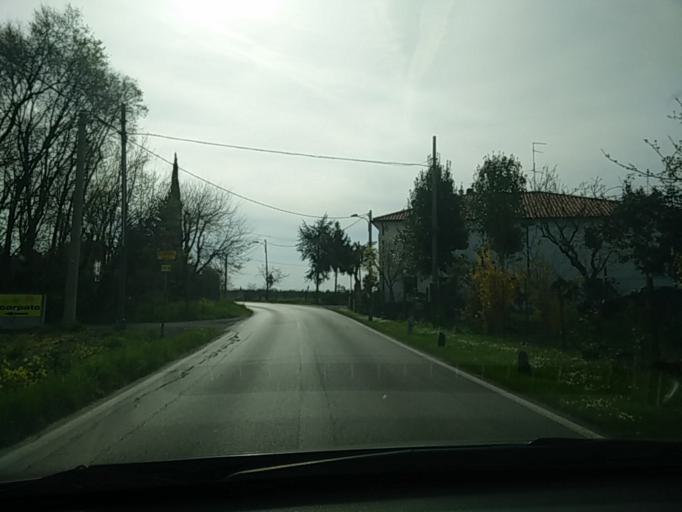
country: IT
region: Emilia-Romagna
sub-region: Provincia di Rimini
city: Santa Giustina
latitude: 44.0818
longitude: 12.4951
